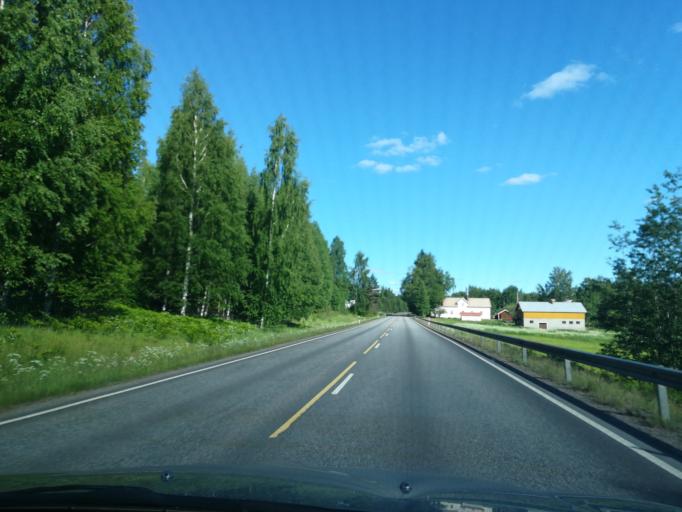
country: FI
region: South Karelia
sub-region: Imatra
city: Ruokolahti
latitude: 61.3731
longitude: 28.6643
